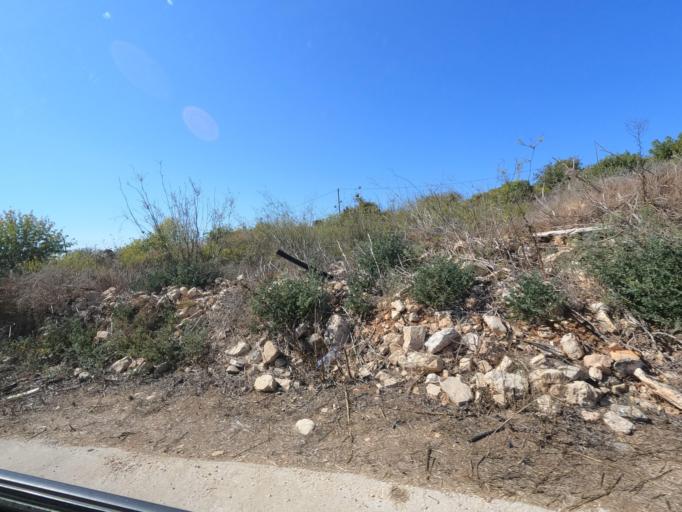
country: CY
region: Pafos
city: Mesogi
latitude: 34.8149
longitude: 32.4765
